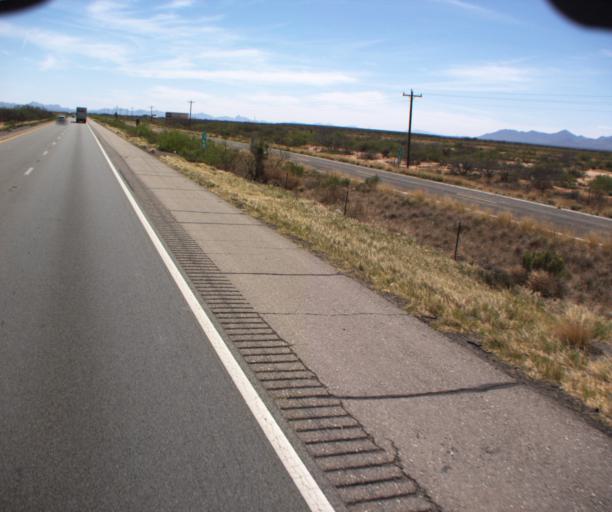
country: US
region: Arizona
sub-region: Cochise County
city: Willcox
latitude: 32.3145
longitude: -109.4302
